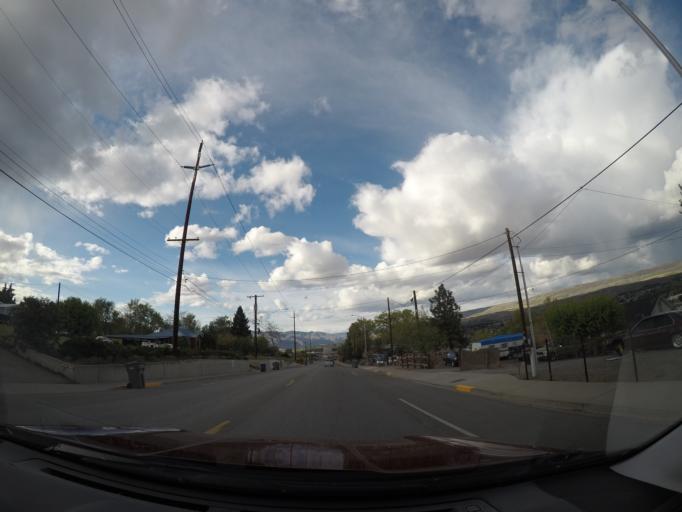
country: US
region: Washington
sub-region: Douglas County
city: East Wenatchee
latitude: 47.4058
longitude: -120.3030
